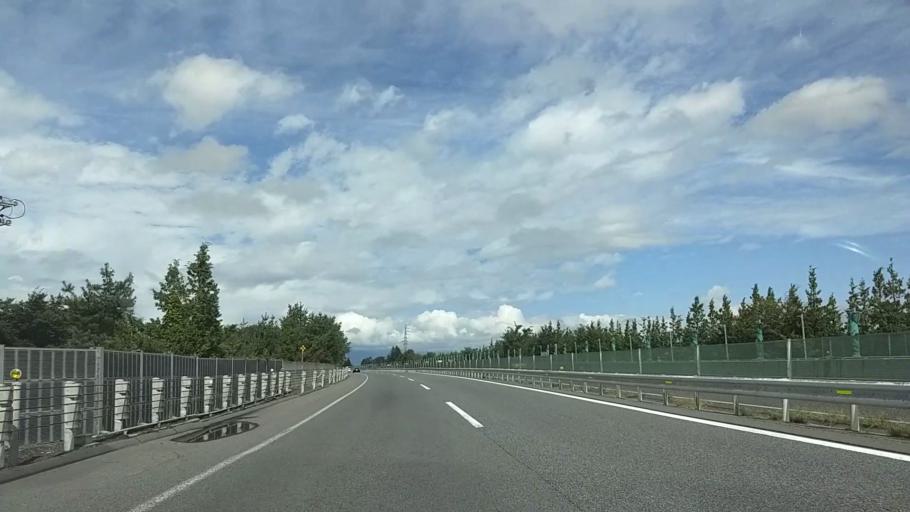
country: JP
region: Nagano
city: Matsumoto
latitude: 36.1999
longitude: 137.9341
